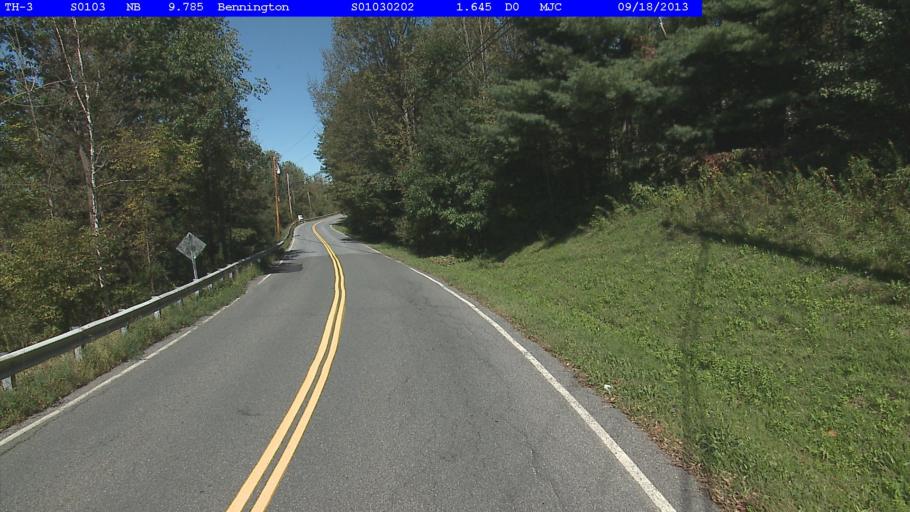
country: US
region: Vermont
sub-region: Bennington County
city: Bennington
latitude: 42.8598
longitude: -73.1753
